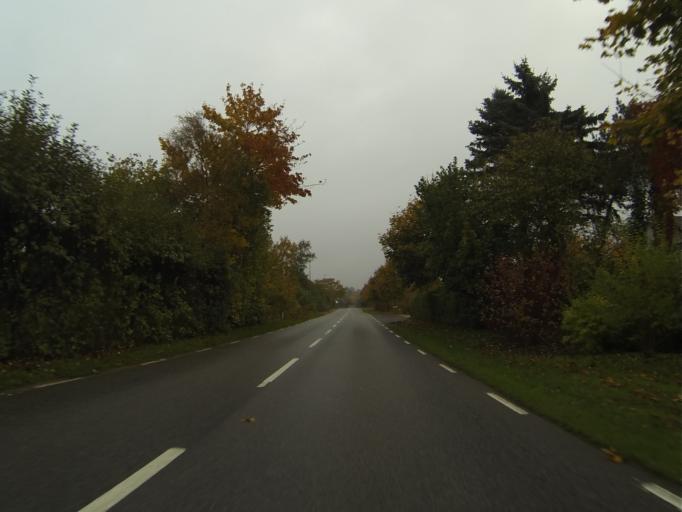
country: SE
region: Skane
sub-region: Hoors Kommun
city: Loberod
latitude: 55.7138
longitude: 13.5208
